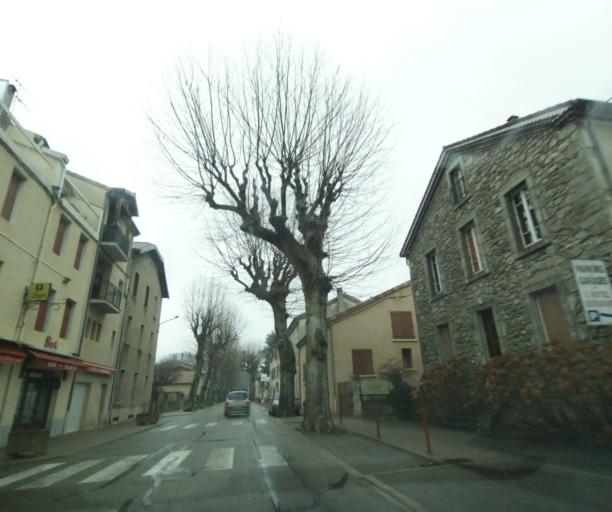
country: FR
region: Rhone-Alpes
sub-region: Departement de l'Ardeche
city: Thueyts
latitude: 44.6745
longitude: 4.2190
